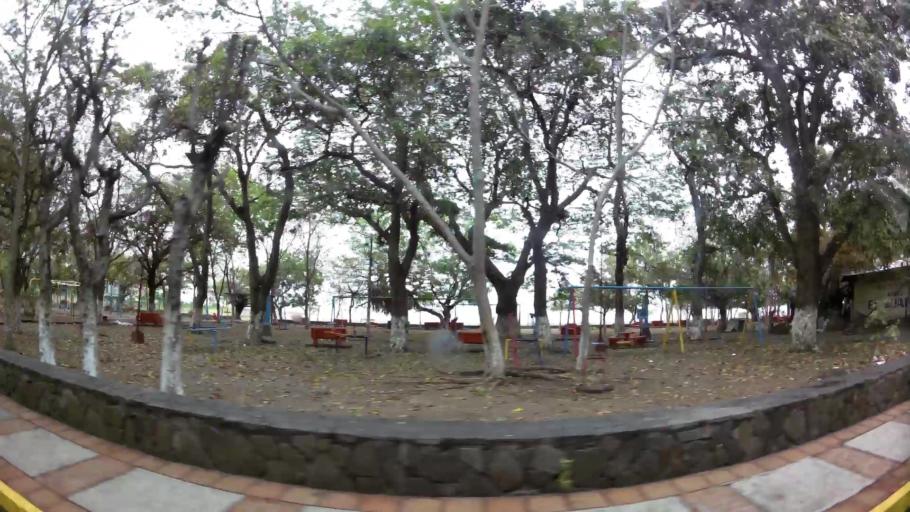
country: NI
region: Granada
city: Granada
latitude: 11.9242
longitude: -85.9409
